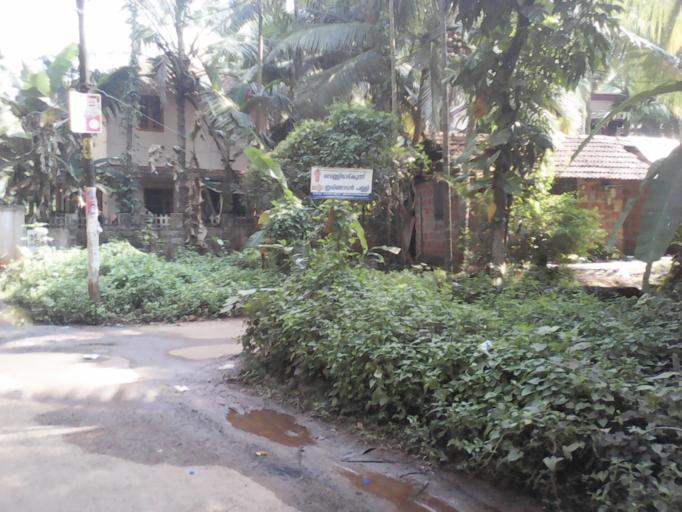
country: IN
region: Kerala
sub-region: Kozhikode
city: Kozhikode
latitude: 11.2823
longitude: 75.8221
